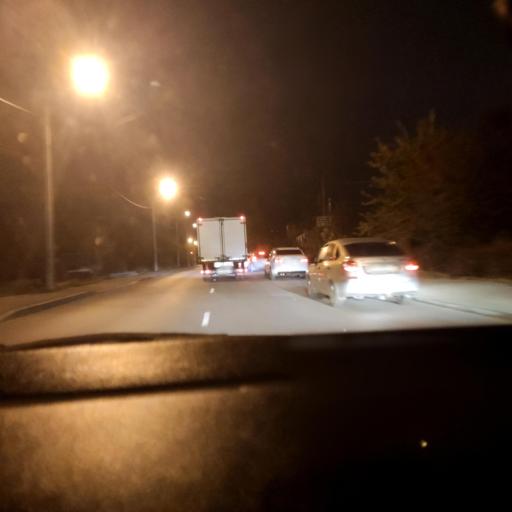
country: RU
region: Voronezj
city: Voronezh
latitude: 51.6924
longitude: 39.1576
